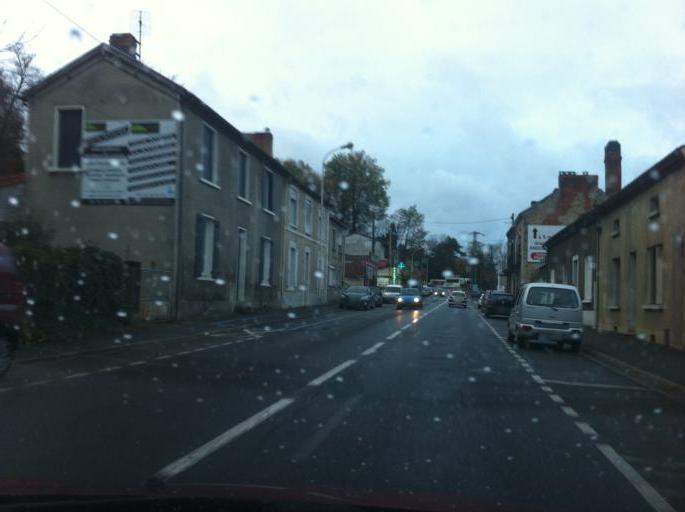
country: FR
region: Aquitaine
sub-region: Departement de la Dordogne
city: Perigueux
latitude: 45.1854
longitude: 0.7002
